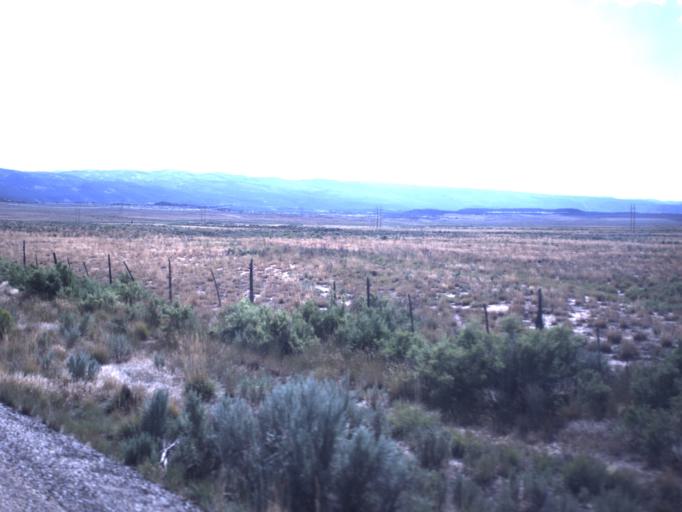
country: US
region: Utah
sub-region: Duchesne County
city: Duchesne
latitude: 40.2323
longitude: -110.7189
